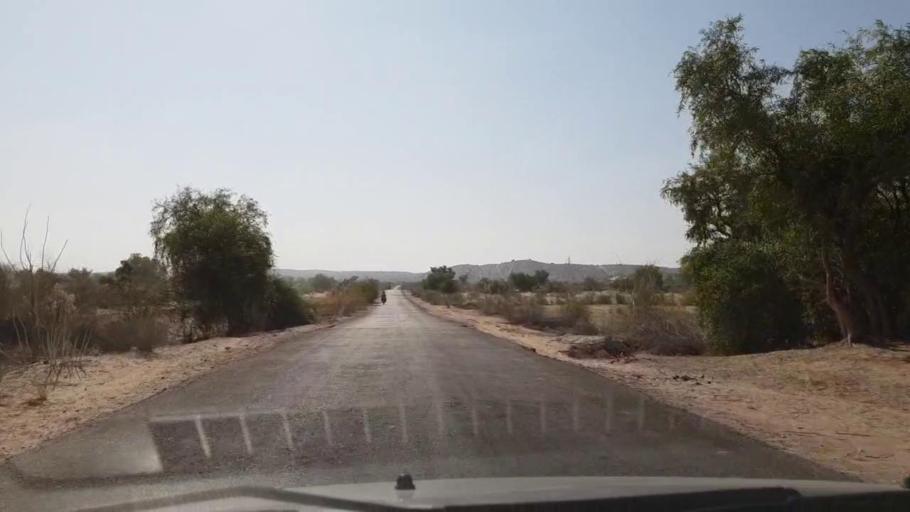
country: PK
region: Sindh
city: Mithi
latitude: 24.6551
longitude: 69.7537
